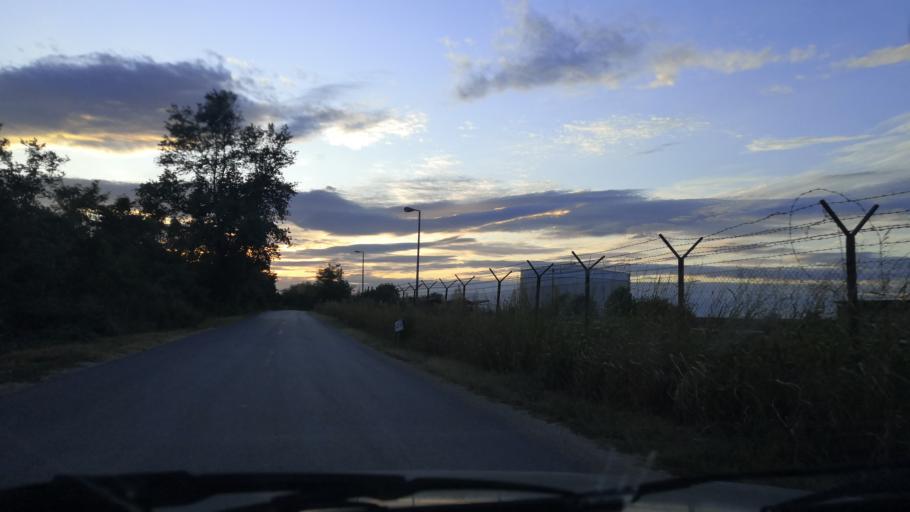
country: RO
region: Mehedinti
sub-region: Comuna Gruia
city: Izvoarele
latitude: 44.2865
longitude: 22.6289
